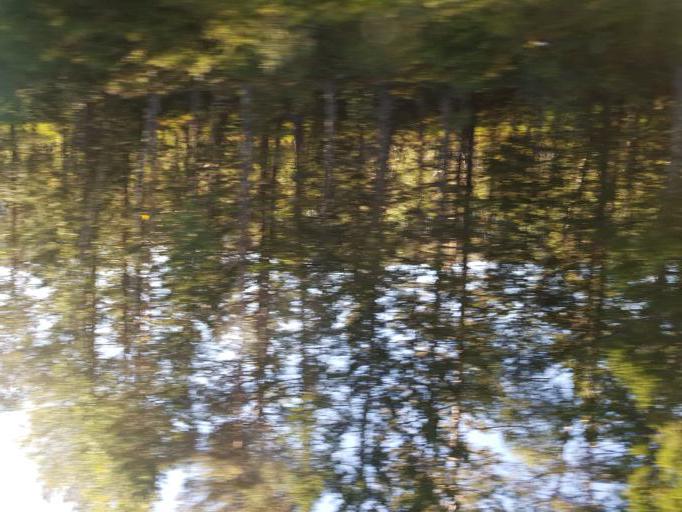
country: NO
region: Sor-Trondelag
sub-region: Afjord
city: A i Afjord
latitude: 63.7844
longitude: 10.2261
